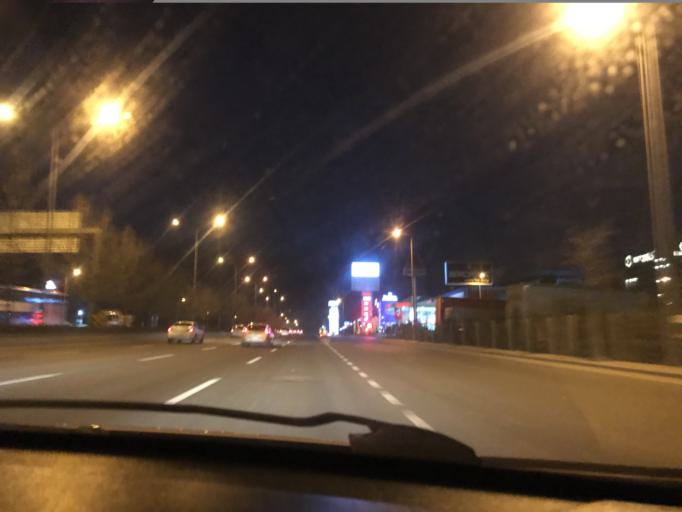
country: TR
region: Ankara
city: Batikent
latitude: 39.9454
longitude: 32.7329
